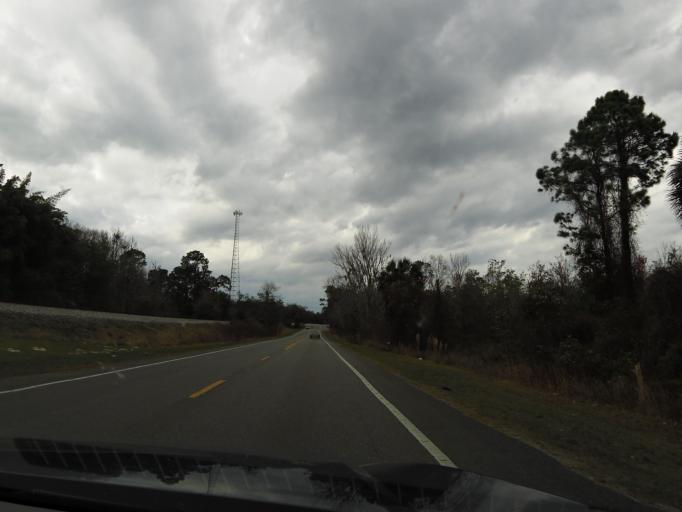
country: US
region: Florida
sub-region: Putnam County
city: Crescent City
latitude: 29.3613
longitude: -81.5063
